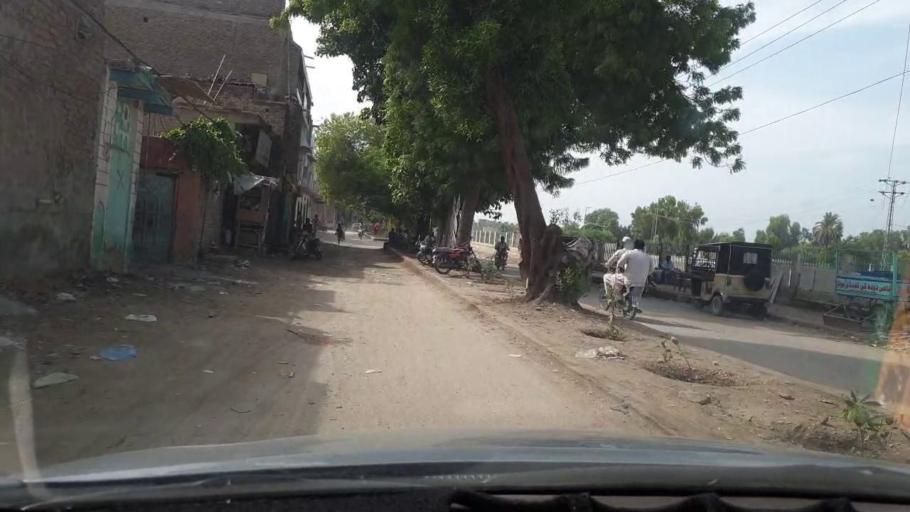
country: PK
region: Sindh
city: Khairpur
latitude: 27.5250
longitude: 68.7555
